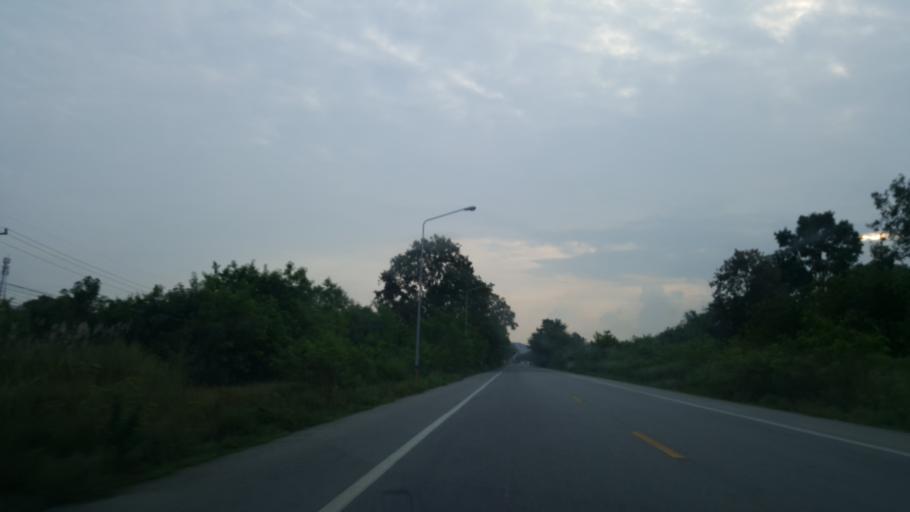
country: TH
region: Chon Buri
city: Sattahip
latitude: 12.7341
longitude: 100.9441
